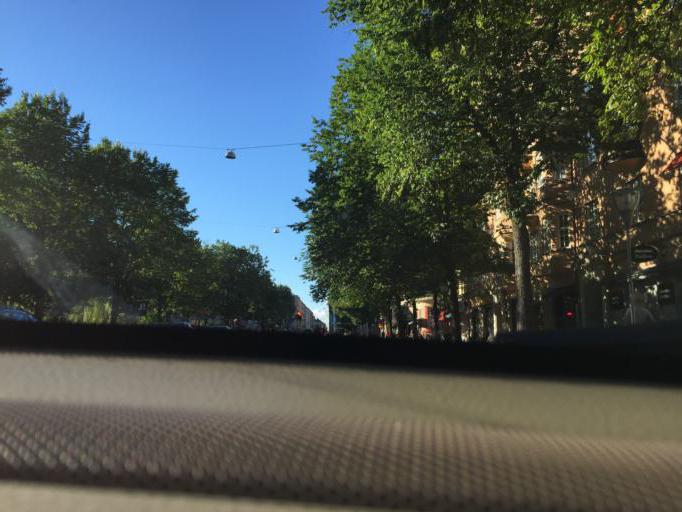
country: SE
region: Stockholm
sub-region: Stockholms Kommun
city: Stockholm
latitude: 59.3425
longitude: 18.0571
